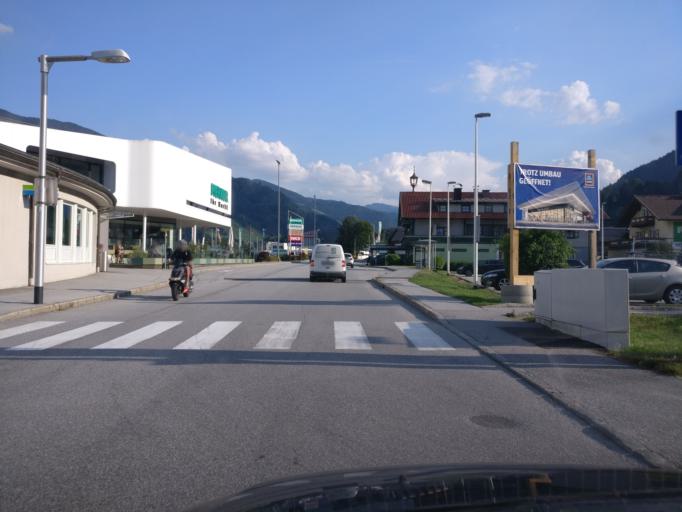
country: AT
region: Salzburg
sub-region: Politischer Bezirk Sankt Johann im Pongau
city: Bischofshofen
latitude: 47.4111
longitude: 13.2166
